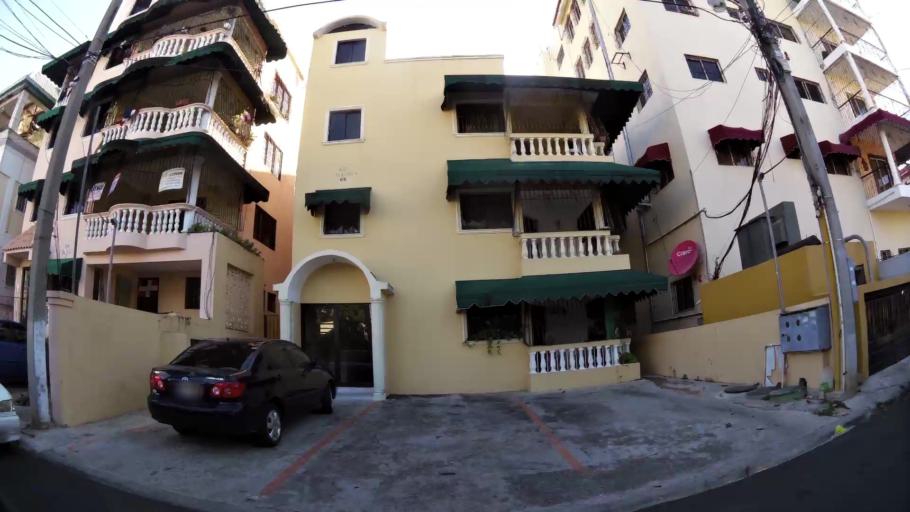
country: DO
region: Nacional
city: Santo Domingo
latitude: 18.4914
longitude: -69.9746
